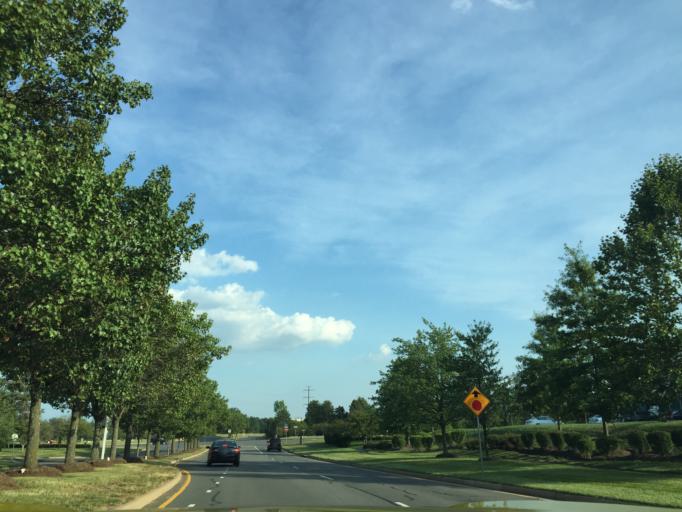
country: US
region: Virginia
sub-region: Loudoun County
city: Sterling
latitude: 39.0196
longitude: -77.4522
